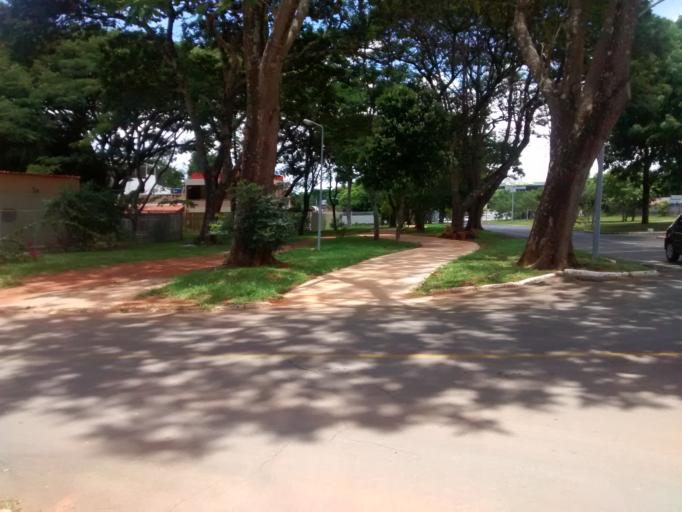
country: BR
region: Federal District
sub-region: Brasilia
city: Brasilia
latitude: -15.8102
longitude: -47.9076
